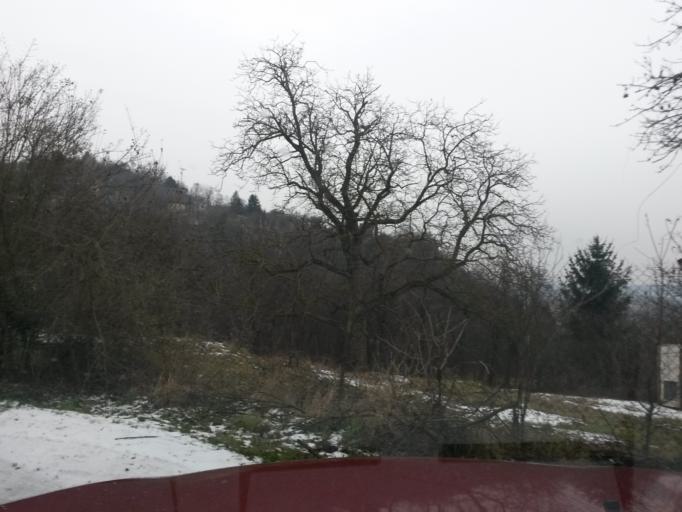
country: SK
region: Kosicky
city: Kosice
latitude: 48.7160
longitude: 21.2827
